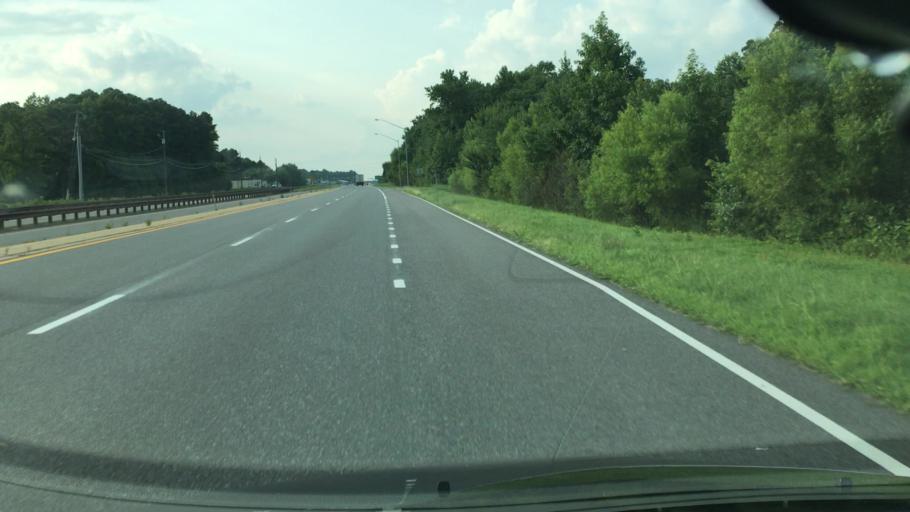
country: US
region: Delaware
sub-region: Sussex County
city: Selbyville
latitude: 38.4234
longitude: -75.2164
